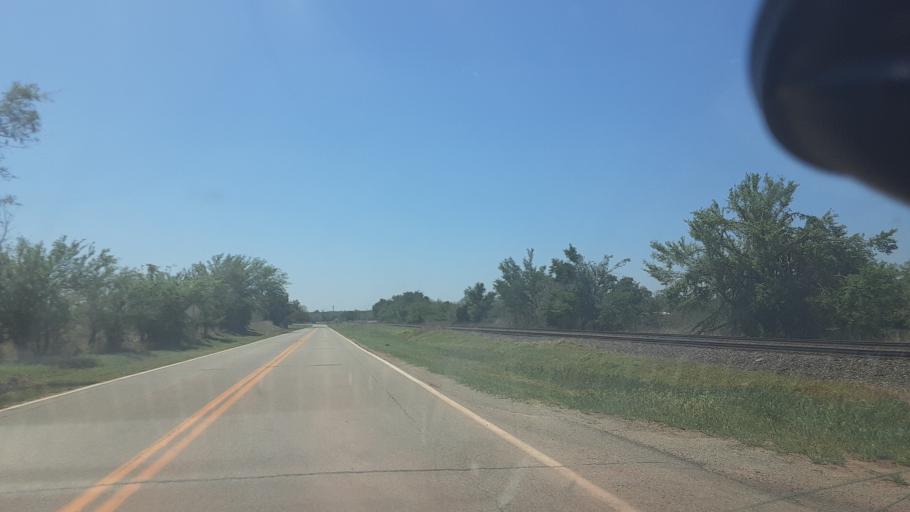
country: US
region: Oklahoma
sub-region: Logan County
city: Guthrie
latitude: 36.0721
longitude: -97.4054
